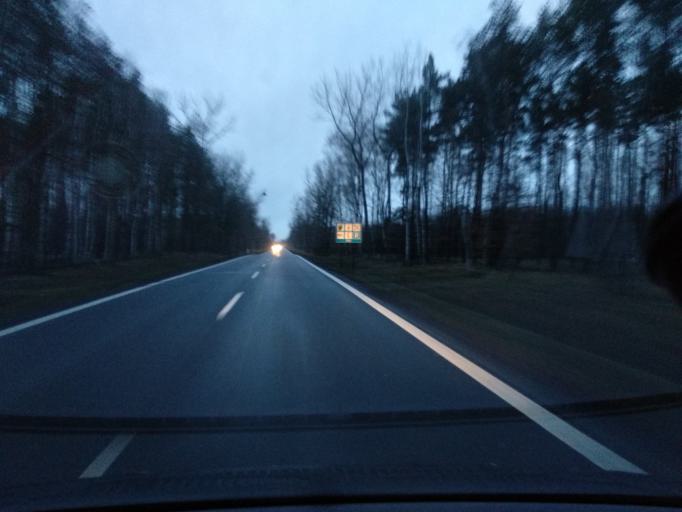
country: PL
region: Lower Silesian Voivodeship
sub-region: Powiat legnicki
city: Prochowice
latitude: 51.2544
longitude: 16.3995
